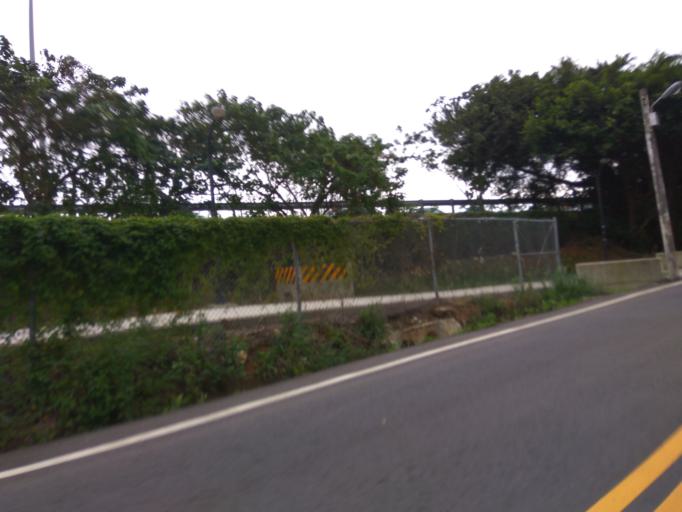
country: TW
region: Taiwan
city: Taoyuan City
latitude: 24.9794
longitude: 121.2268
